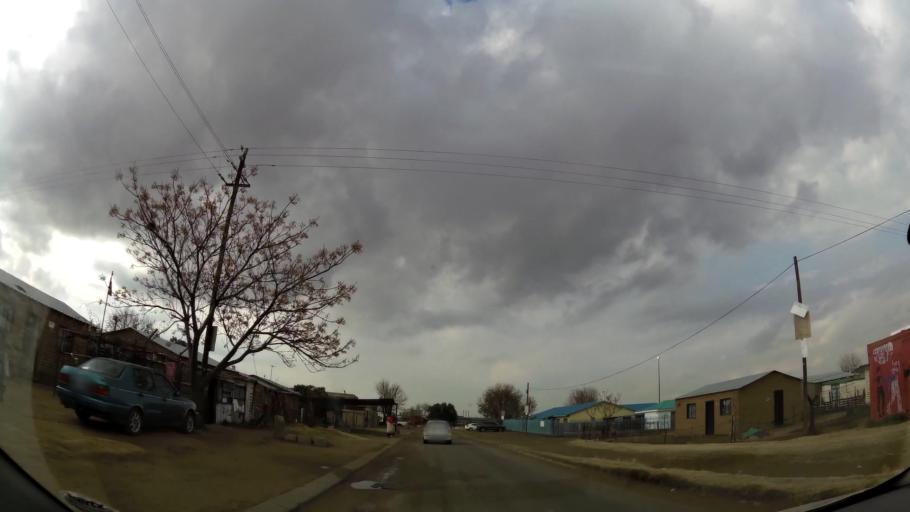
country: ZA
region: Orange Free State
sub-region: Fezile Dabi District Municipality
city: Sasolburg
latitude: -26.8456
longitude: 27.8640
